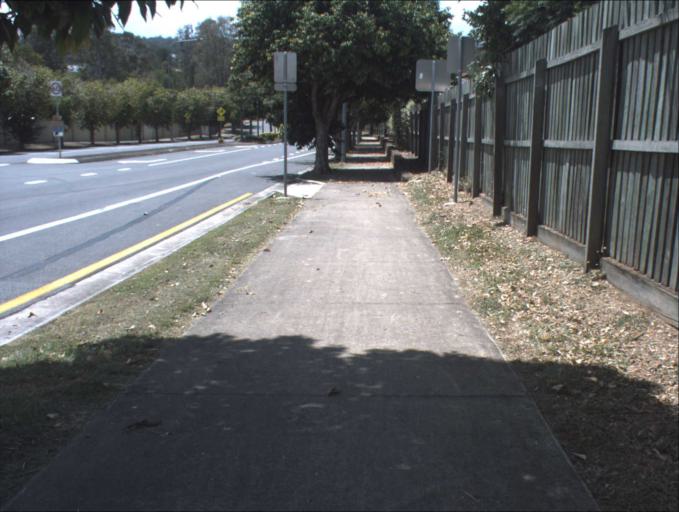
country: AU
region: Queensland
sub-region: Logan
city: Slacks Creek
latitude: -27.6421
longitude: 153.1455
